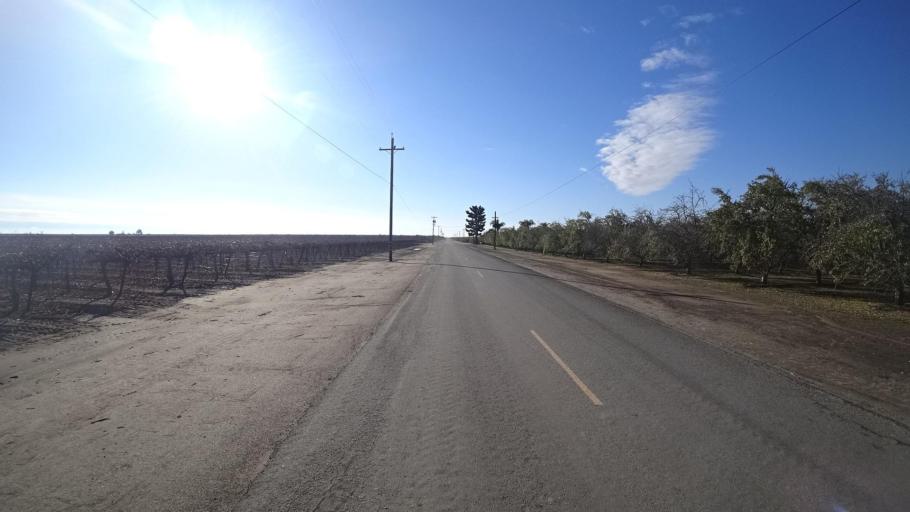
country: US
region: California
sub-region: Kern County
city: McFarland
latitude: 35.7081
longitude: -119.3119
